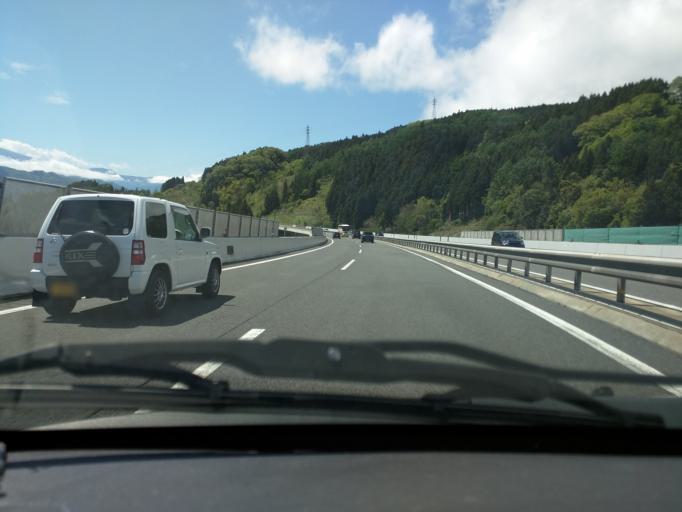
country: JP
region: Nagano
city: Nakano
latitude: 36.7838
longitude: 138.3179
